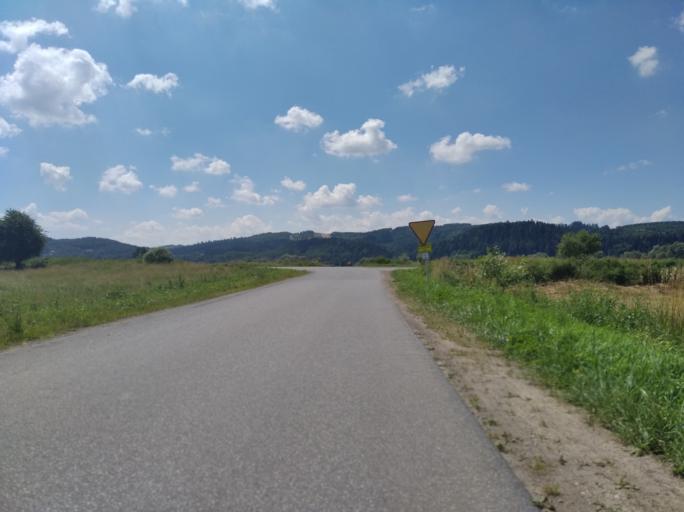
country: PL
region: Subcarpathian Voivodeship
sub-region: Powiat brzozowski
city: Dydnia
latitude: 49.7034
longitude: 22.2091
